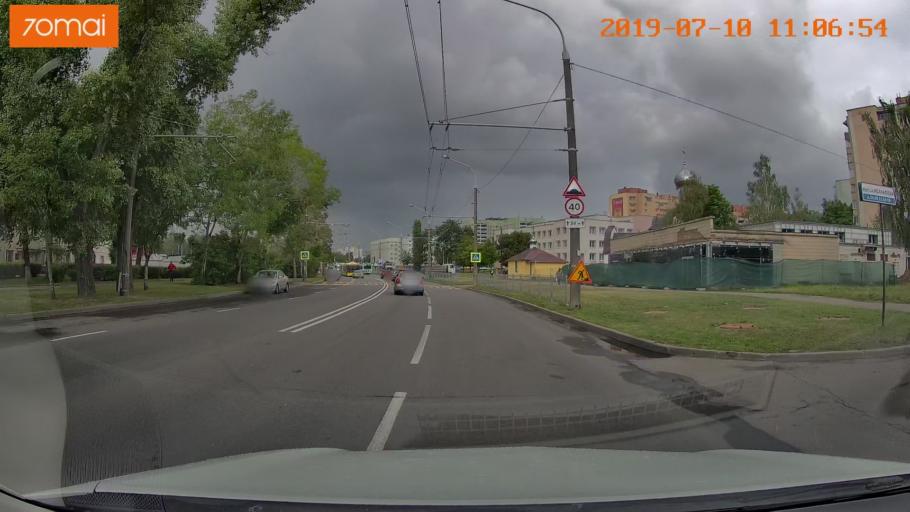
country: BY
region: Minsk
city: Syenitsa
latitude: 53.8493
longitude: 27.5407
